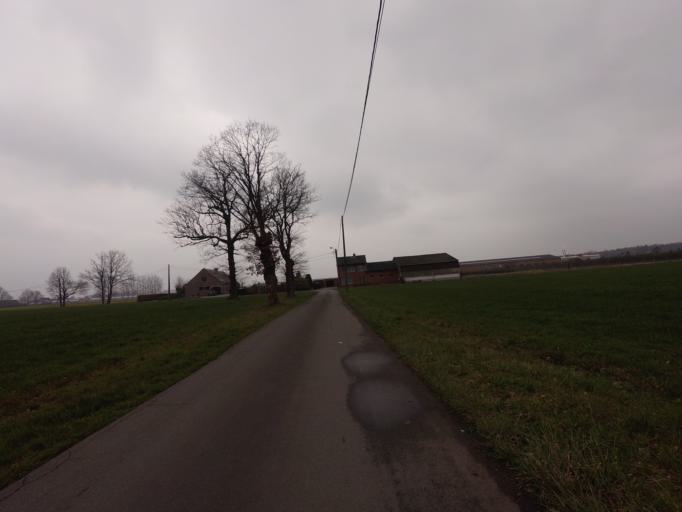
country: BE
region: Flanders
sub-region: Provincie Antwerpen
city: Putte
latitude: 51.0755
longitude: 4.5921
